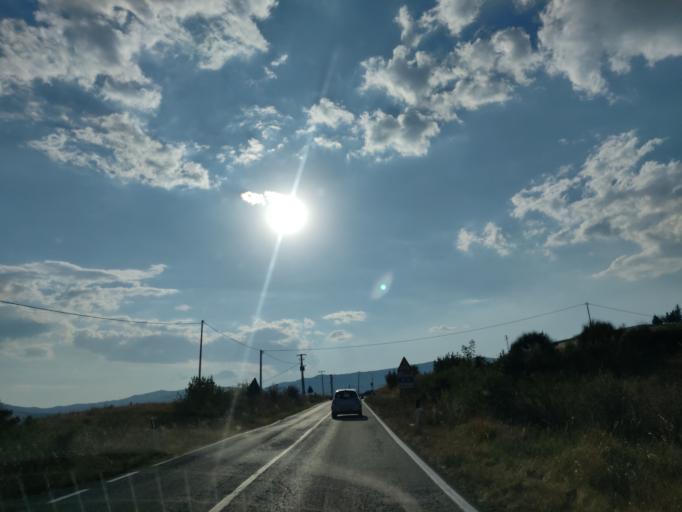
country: IT
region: Tuscany
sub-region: Provincia di Siena
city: Piancastagnaio
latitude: 42.8348
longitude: 11.7133
